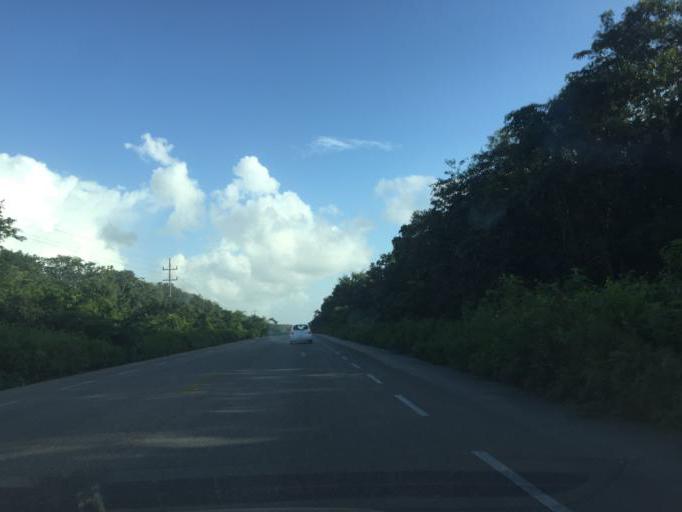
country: MX
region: Quintana Roo
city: Coba
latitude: 20.4955
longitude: -87.7077
